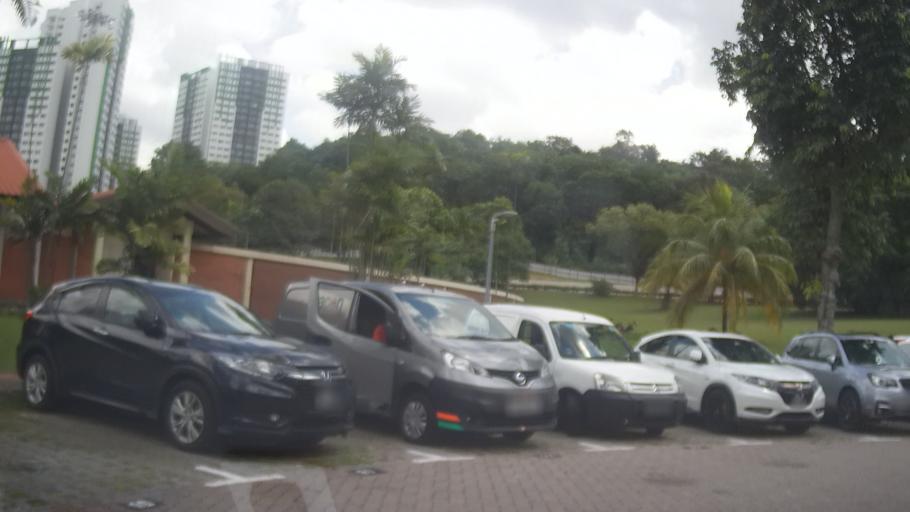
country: MY
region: Johor
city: Johor Bahru
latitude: 1.4348
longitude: 103.7798
